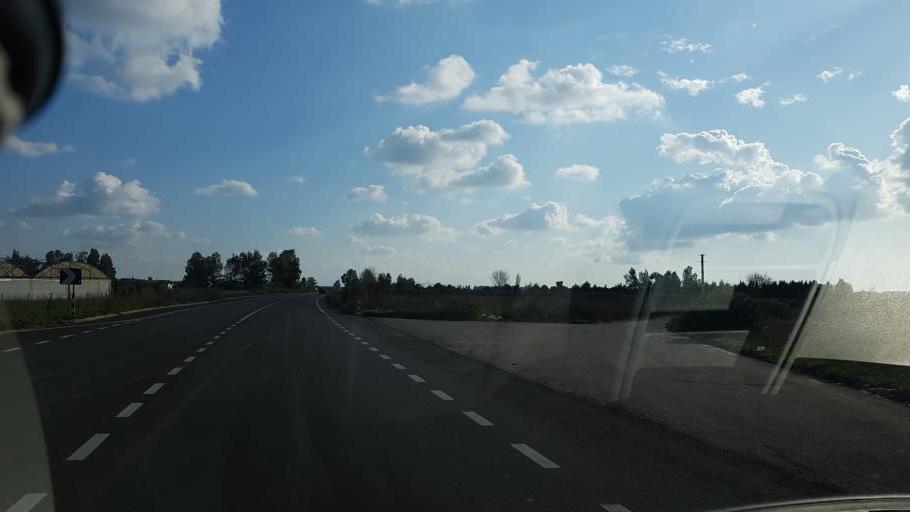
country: IT
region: Apulia
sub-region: Provincia di Lecce
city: Veglie
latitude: 40.3463
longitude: 17.9748
